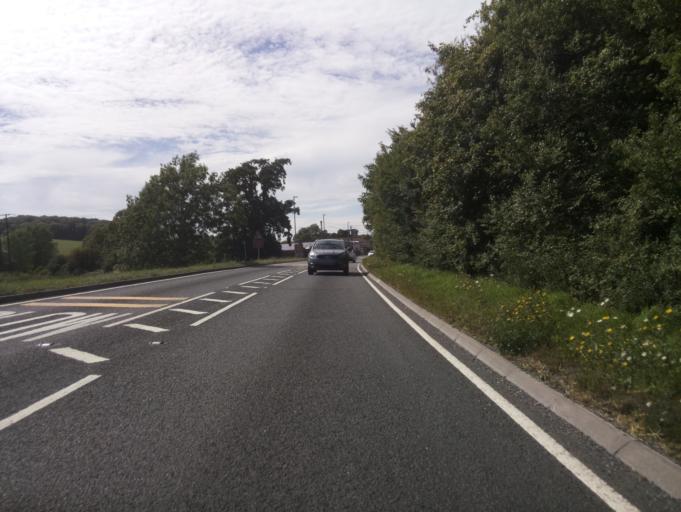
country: GB
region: England
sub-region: Dorset
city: Dorchester
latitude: 50.7444
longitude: -2.5102
